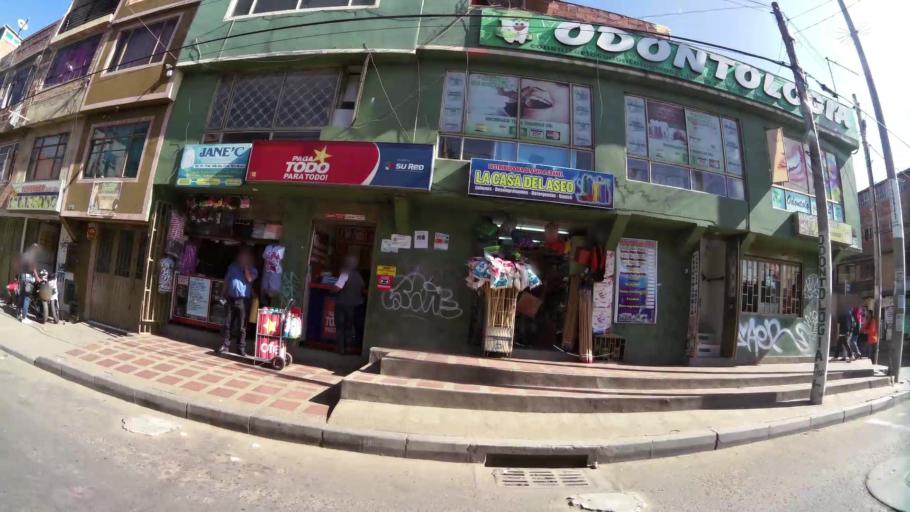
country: CO
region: Cundinamarca
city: Soacha
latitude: 4.5467
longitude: -74.1394
